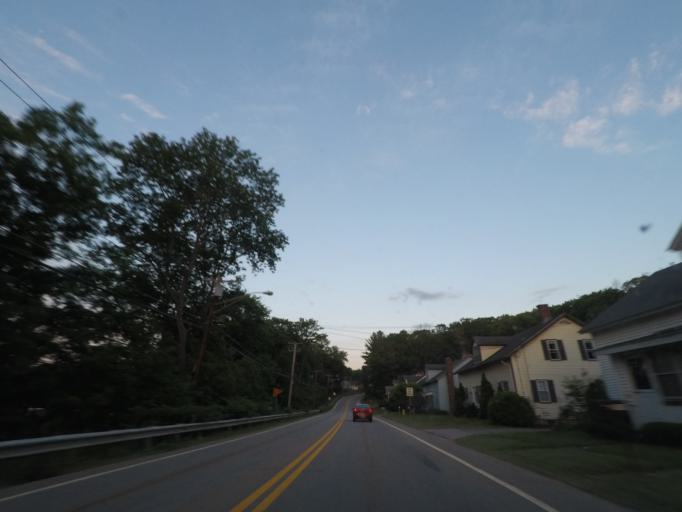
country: US
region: Massachusetts
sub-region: Worcester County
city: Southbridge
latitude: 42.0642
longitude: -72.0079
